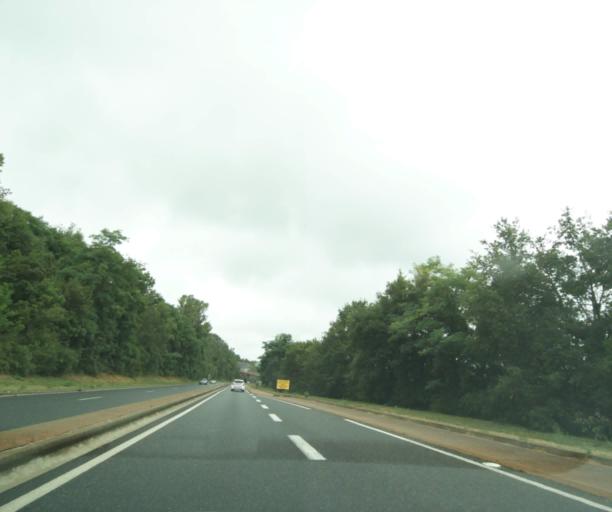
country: FR
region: Midi-Pyrenees
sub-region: Departement de l'Aveyron
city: Olemps
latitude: 44.3417
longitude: 2.5611
